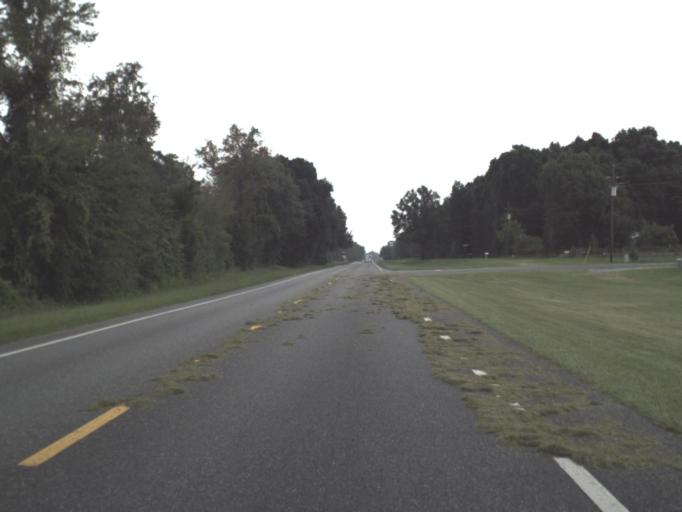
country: US
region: Florida
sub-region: Alachua County
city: High Springs
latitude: 29.8955
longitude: -82.6092
